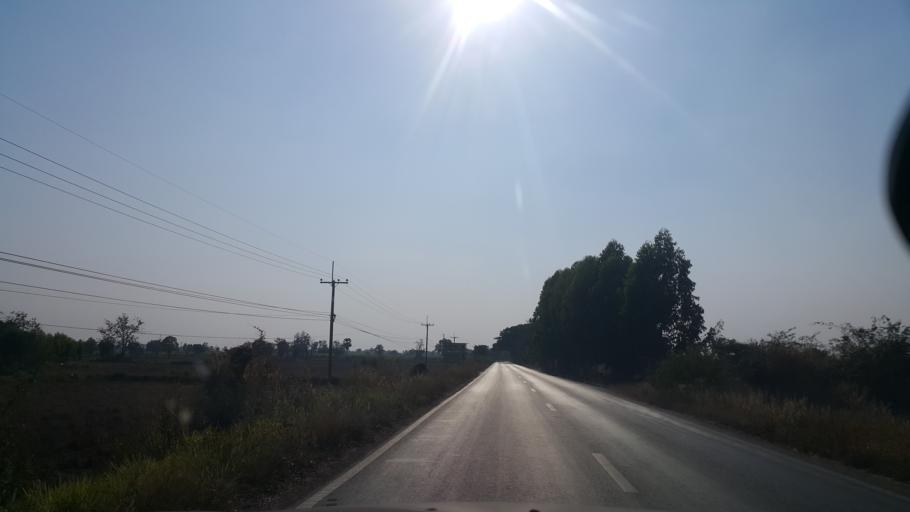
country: TH
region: Nakhon Ratchasima
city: Phimai
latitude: 15.1866
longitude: 102.4218
